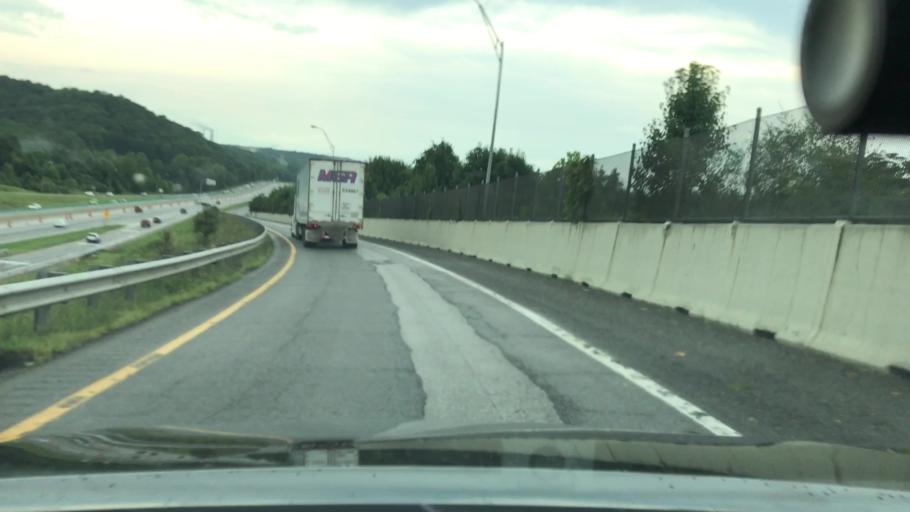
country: US
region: West Virginia
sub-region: Putnam County
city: Teays Valley
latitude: 38.4534
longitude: -81.9016
